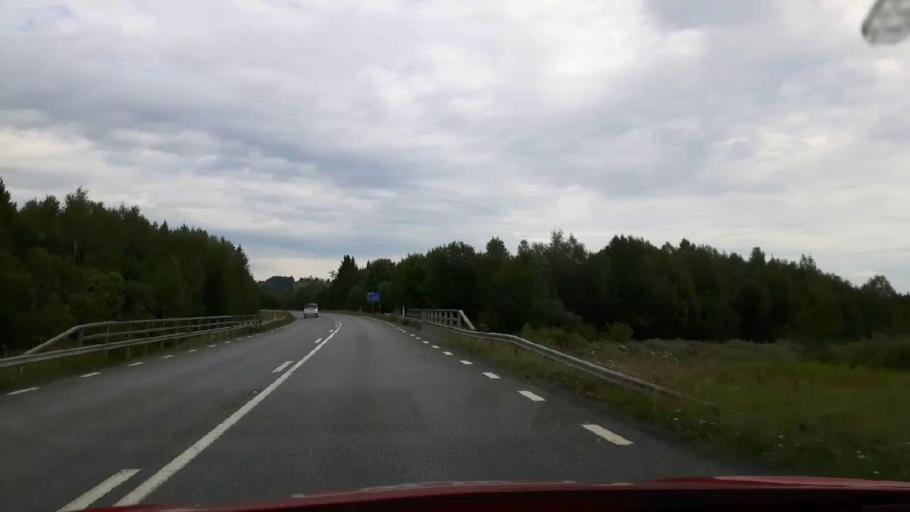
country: SE
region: Jaemtland
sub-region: Stroemsunds Kommun
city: Stroemsund
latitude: 63.5442
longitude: 15.3704
